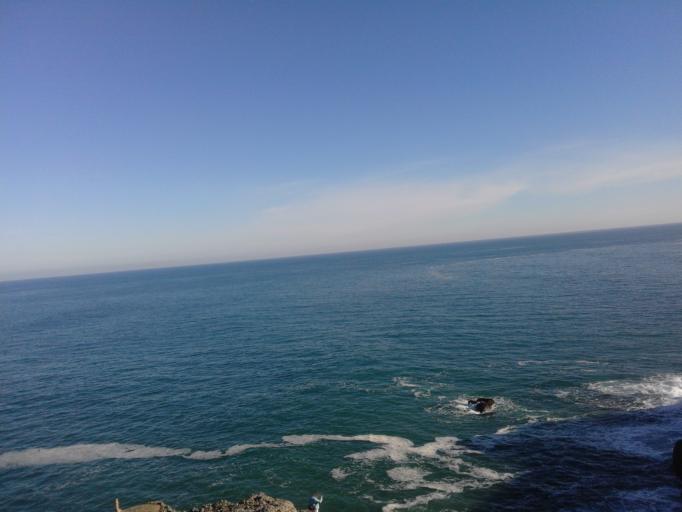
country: ES
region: Cantabria
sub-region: Provincia de Cantabria
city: Arnuero
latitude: 43.5123
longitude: -3.5823
